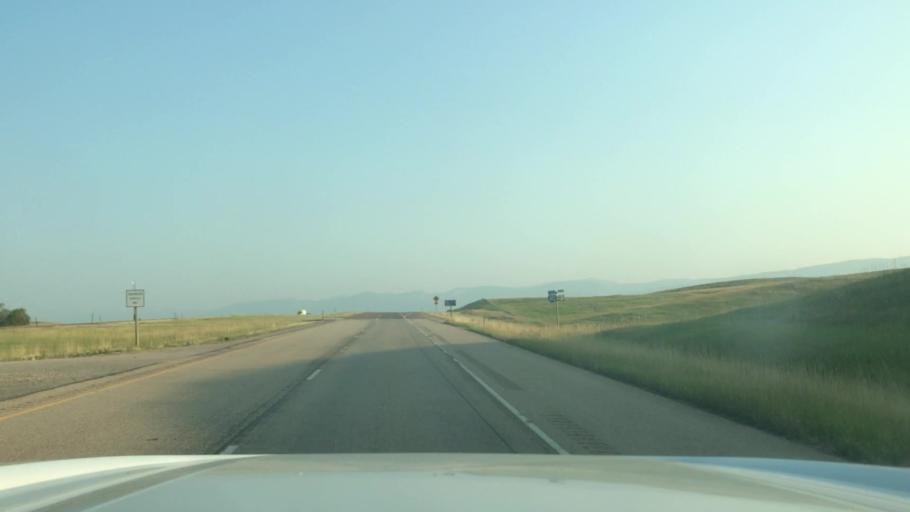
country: US
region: Wyoming
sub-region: Sheridan County
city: Sheridan
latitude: 45.0017
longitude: -107.2986
